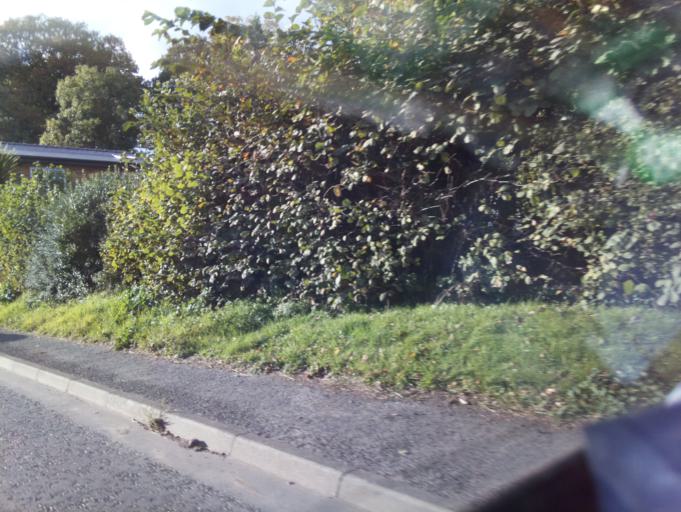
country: GB
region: England
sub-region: Herefordshire
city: Credenhill
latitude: 52.0722
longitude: -2.7908
